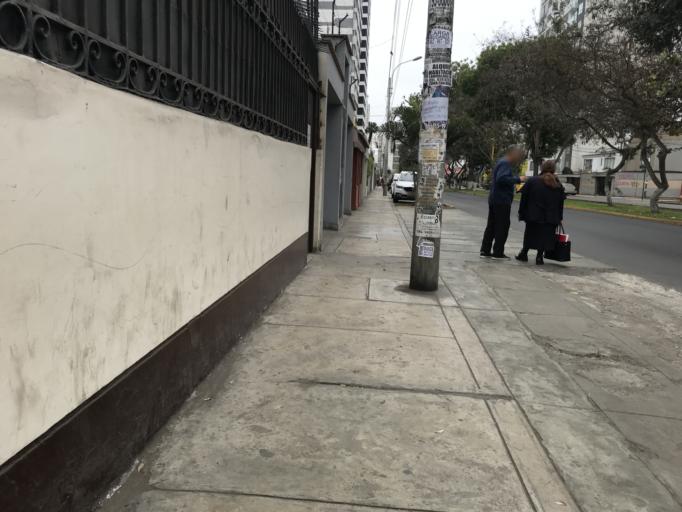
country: PE
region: Lima
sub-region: Lima
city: San Isidro
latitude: -12.0767
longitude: -77.0731
